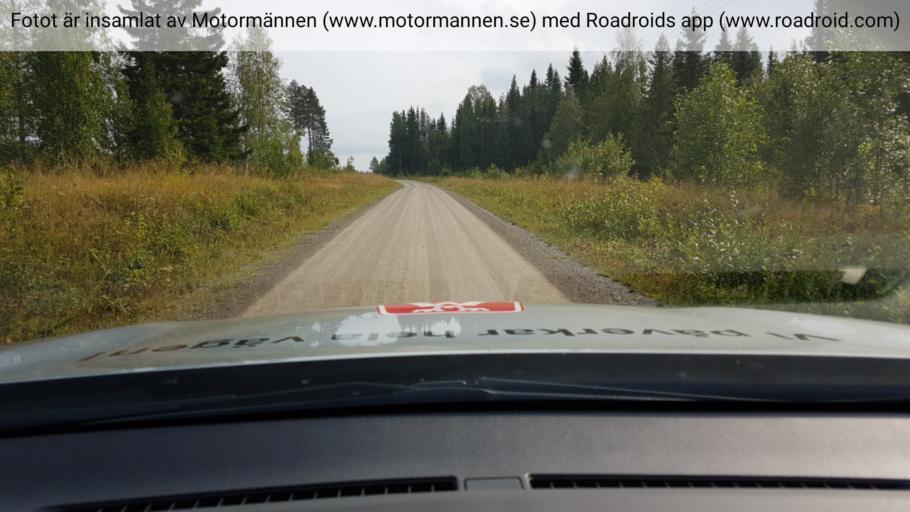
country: SE
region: Jaemtland
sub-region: Stroemsunds Kommun
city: Stroemsund
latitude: 63.7540
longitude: 15.3705
